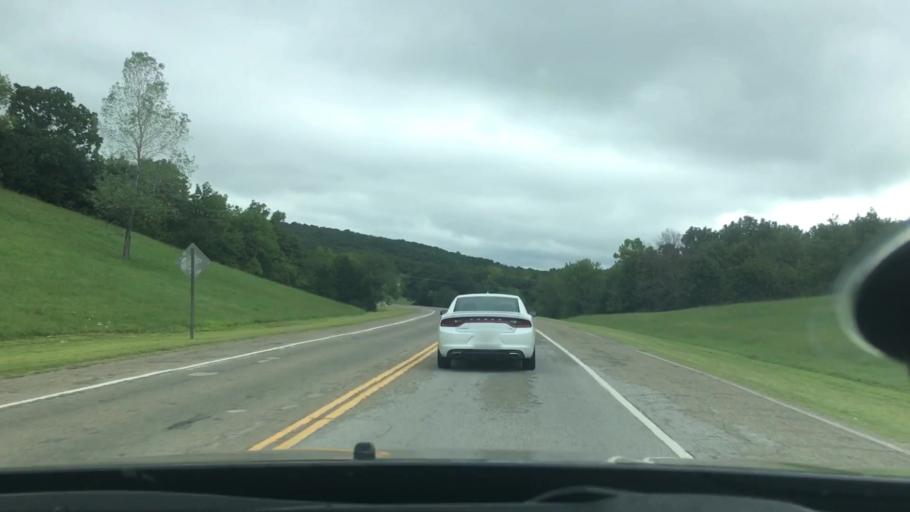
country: US
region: Oklahoma
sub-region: Sequoyah County
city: Vian
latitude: 35.5131
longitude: -94.9694
